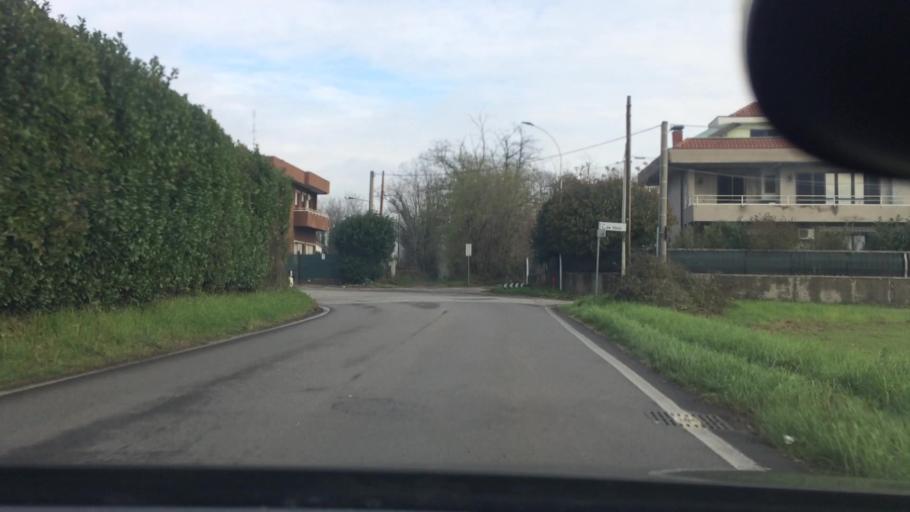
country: IT
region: Lombardy
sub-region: Citta metropolitana di Milano
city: Cerro Maggiore
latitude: 45.6027
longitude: 8.9535
